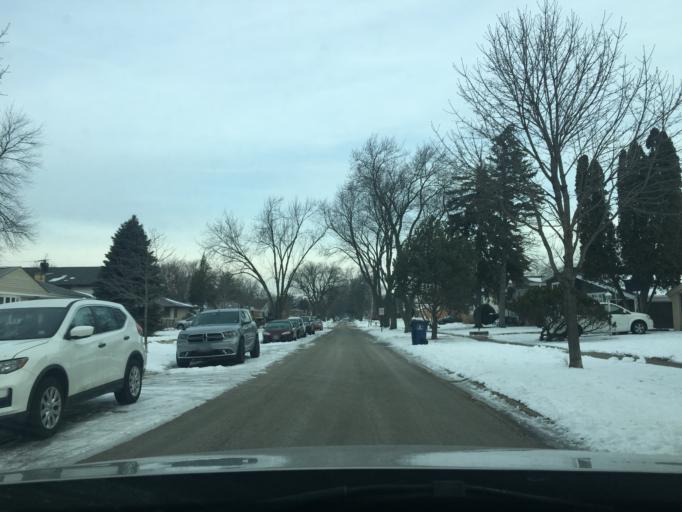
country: US
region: Illinois
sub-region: Cook County
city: Rosemont
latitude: 42.0140
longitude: -87.8931
